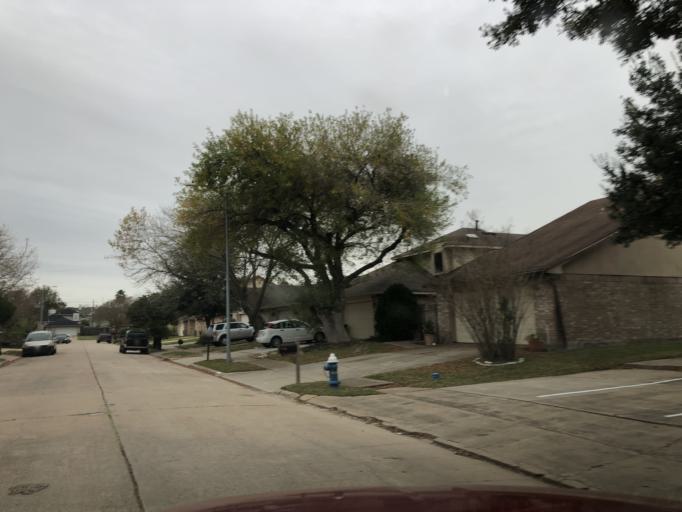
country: US
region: Texas
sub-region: Fort Bend County
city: Missouri City
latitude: 29.6408
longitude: -95.5300
